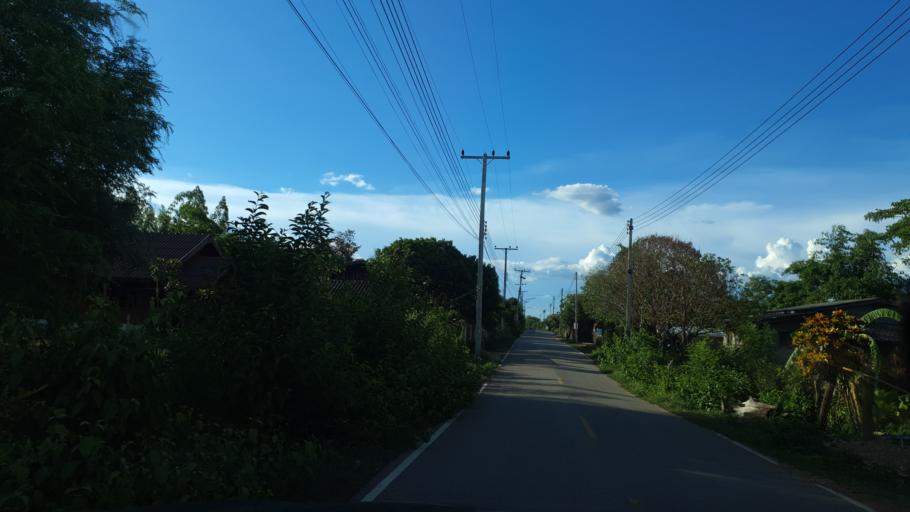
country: TH
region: Lampang
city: Sop Prap
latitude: 17.8833
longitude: 99.3115
